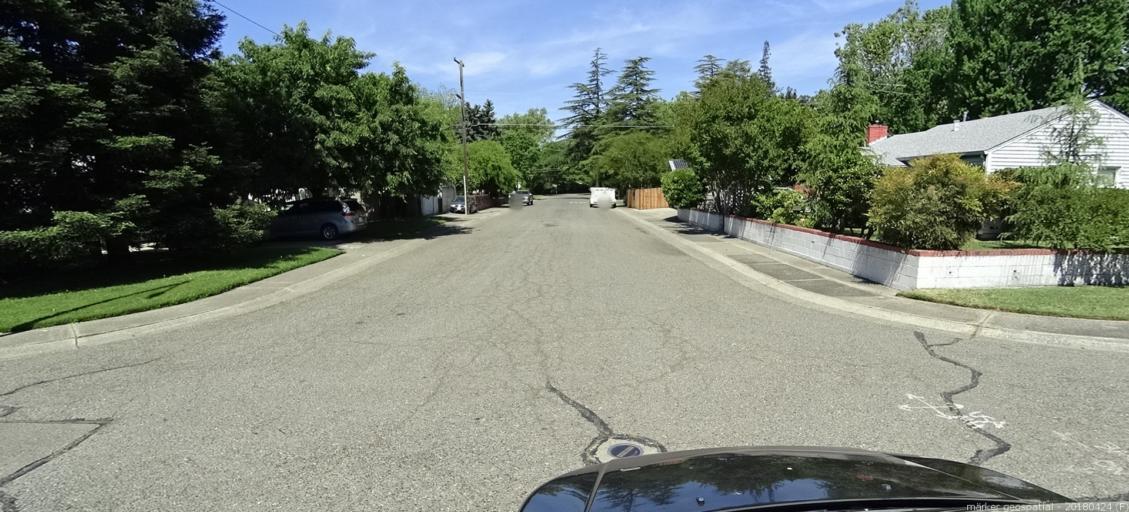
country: US
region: California
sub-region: Yolo County
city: West Sacramento
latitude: 38.5672
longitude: -121.5312
